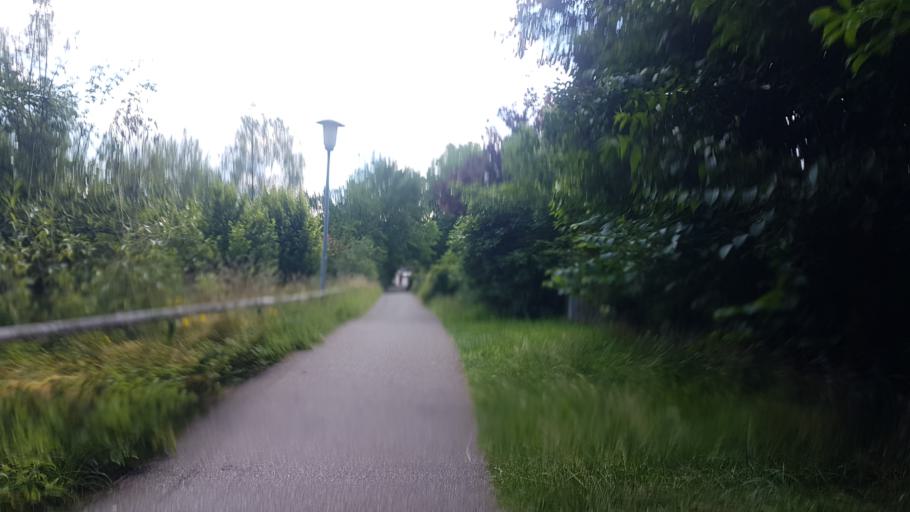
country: DE
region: Bavaria
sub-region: Upper Bavaria
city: Eichstaett
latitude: 48.8924
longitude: 11.1640
